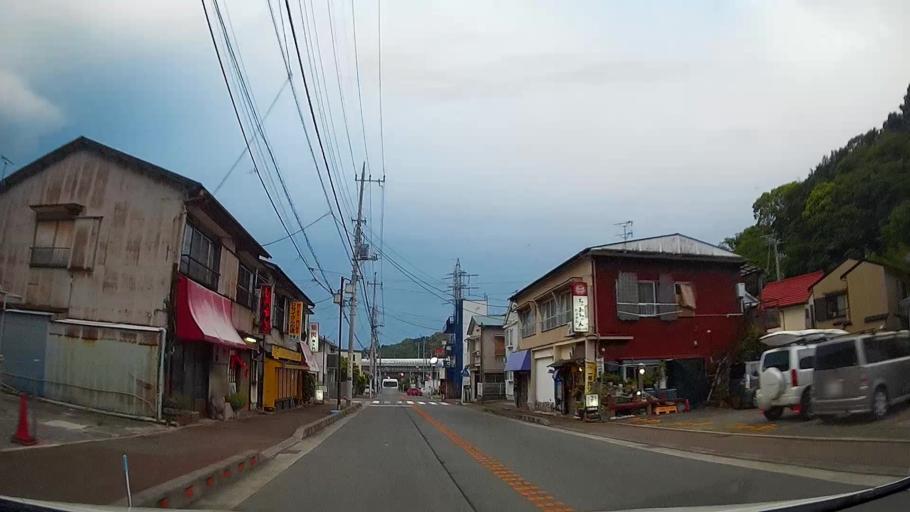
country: JP
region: Kanagawa
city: Yugawara
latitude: 35.1411
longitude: 139.0918
